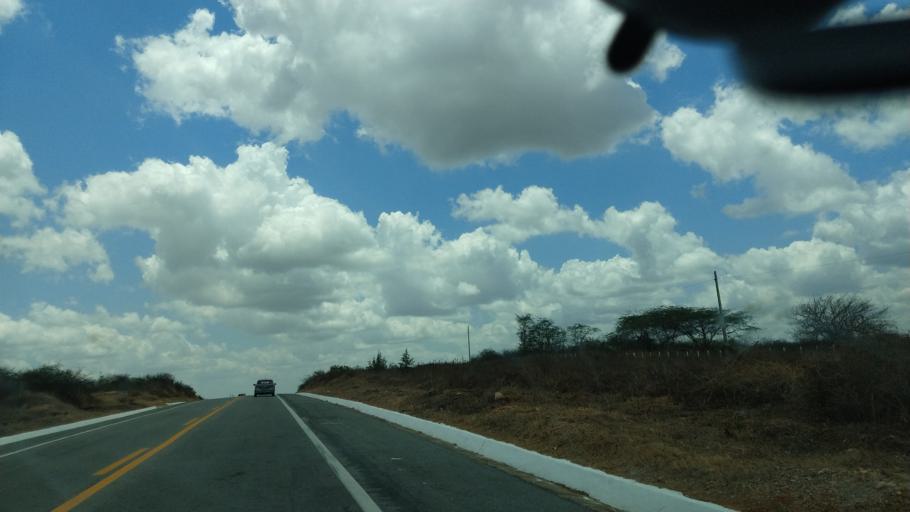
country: BR
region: Rio Grande do Norte
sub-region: Cerro Cora
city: Cerro Cora
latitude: -6.1899
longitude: -36.2268
